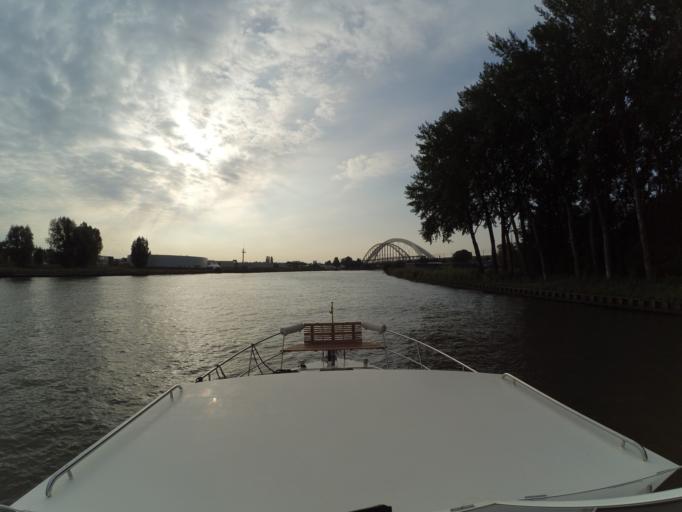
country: NL
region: Utrecht
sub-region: Stichtse Vecht
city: Maarssen
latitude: 52.1141
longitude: 5.0743
